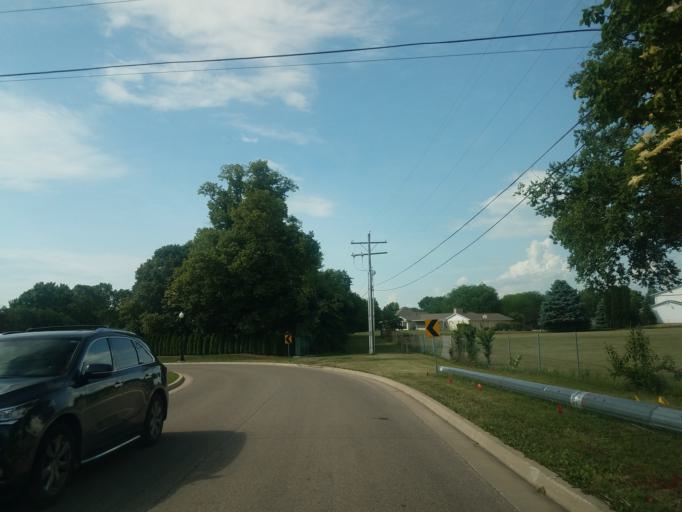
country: US
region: Illinois
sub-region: McLean County
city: Bloomington
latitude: 40.4811
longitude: -88.9627
